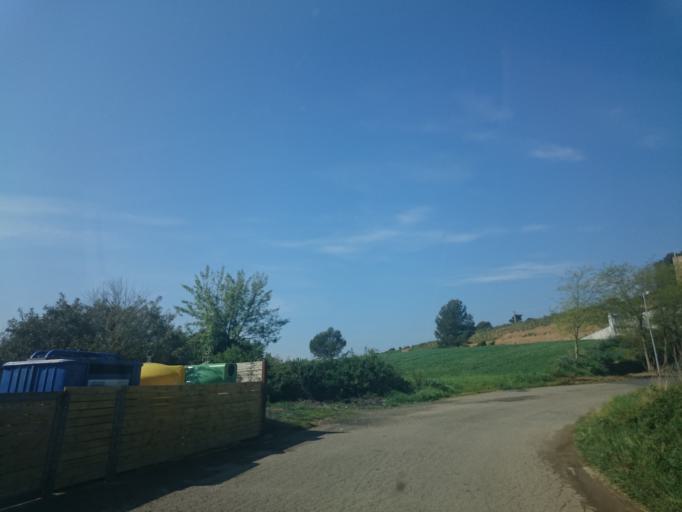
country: ES
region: Catalonia
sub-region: Provincia de Girona
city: Cervia de Ter
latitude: 42.0944
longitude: 2.8940
